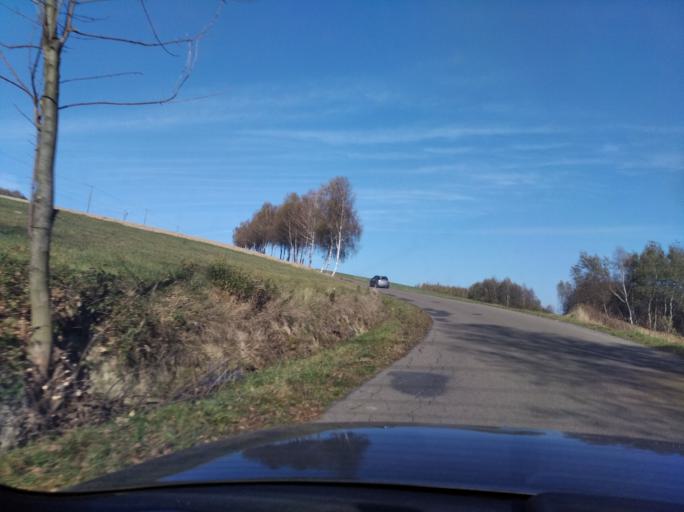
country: PL
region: Subcarpathian Voivodeship
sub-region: Powiat ropczycko-sedziszowski
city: Wielopole Skrzynskie
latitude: 49.9117
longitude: 21.5683
